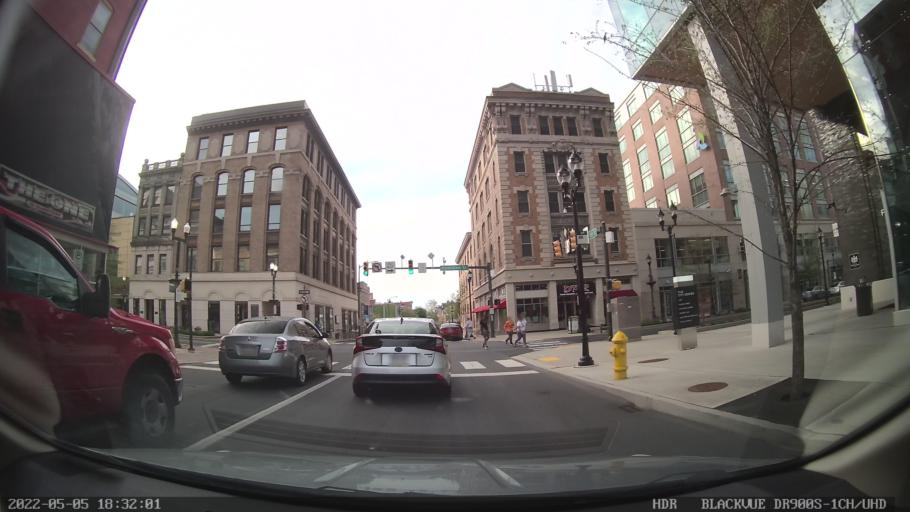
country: US
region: Pennsylvania
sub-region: Lehigh County
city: Allentown
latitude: 40.6016
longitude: -75.4729
